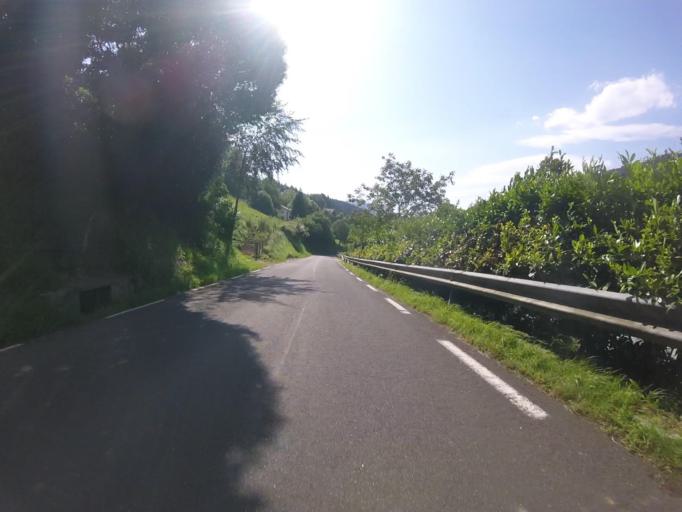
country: ES
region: Basque Country
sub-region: Provincia de Guipuzcoa
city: Alquiza
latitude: 43.1694
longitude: -2.1031
